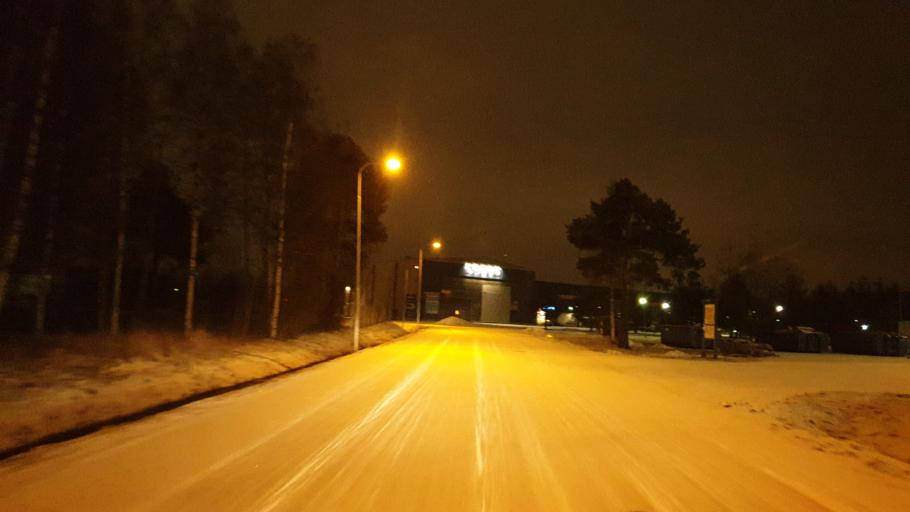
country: FI
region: Northern Ostrobothnia
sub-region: Oulu
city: Oulu
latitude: 64.9937
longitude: 25.4499
